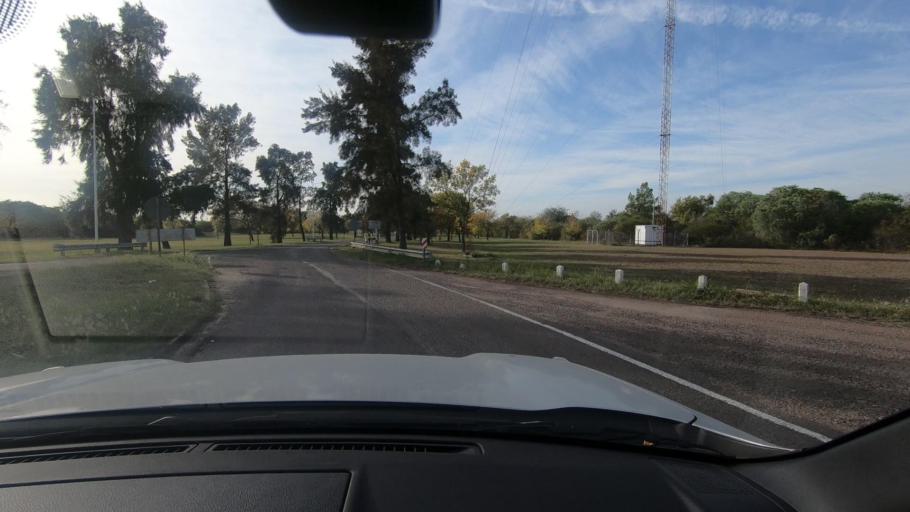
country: AR
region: Entre Rios
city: Colon
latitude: -32.2444
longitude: -58.1863
